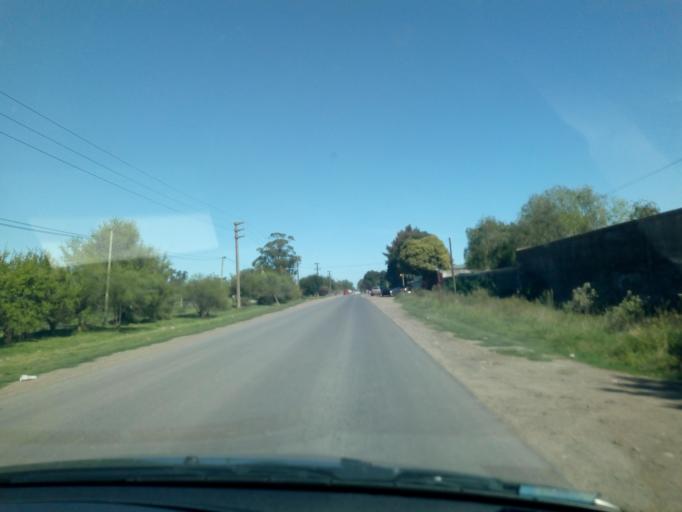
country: AR
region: Buenos Aires
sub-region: Partido de La Plata
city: La Plata
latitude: -35.0091
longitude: -58.0261
